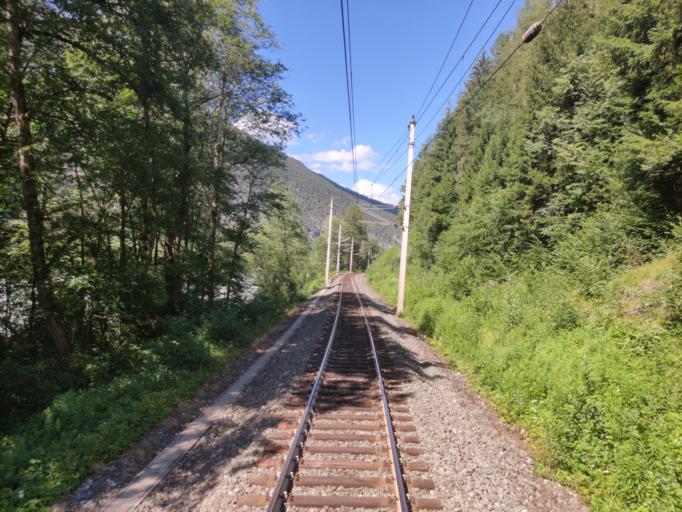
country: AT
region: Tyrol
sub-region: Politischer Bezirk Imst
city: Imsterberg
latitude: 47.2029
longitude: 10.6860
